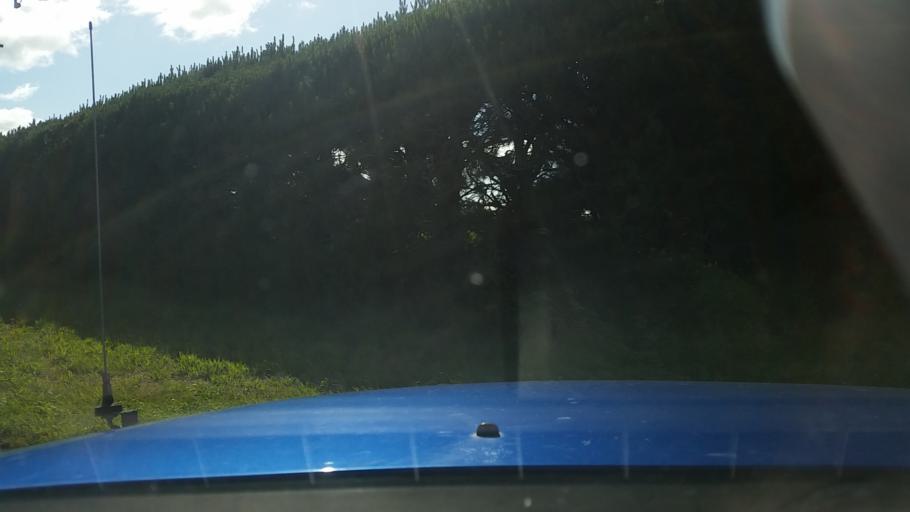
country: NZ
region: Canterbury
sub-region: Ashburton District
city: Rakaia
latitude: -43.8498
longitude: 172.0978
